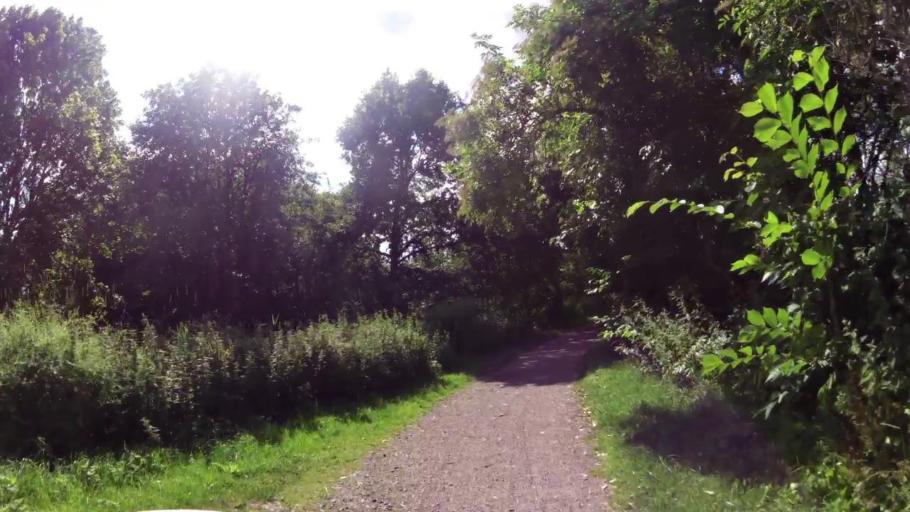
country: SE
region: OEstergoetland
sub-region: Linkopings Kommun
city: Berg
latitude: 58.4946
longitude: 15.5110
